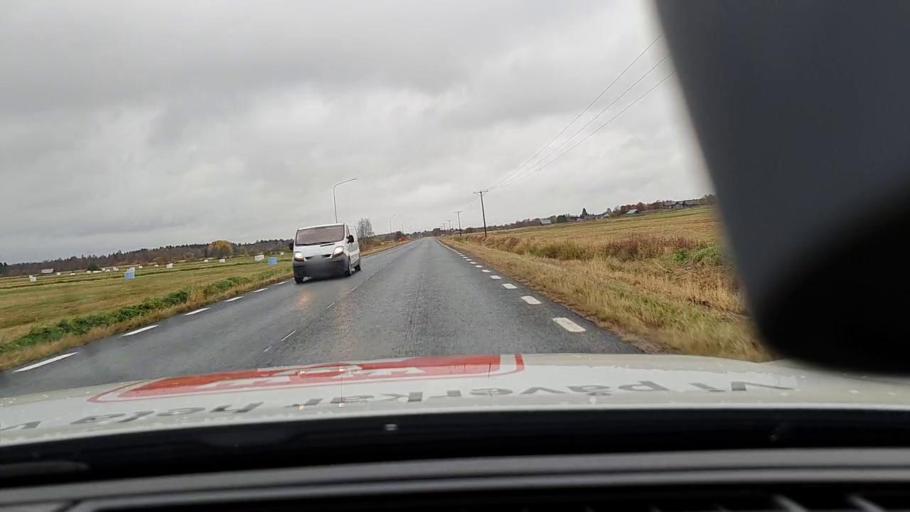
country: FI
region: Lapland
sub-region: Kemi-Tornio
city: Tornio
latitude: 65.9828
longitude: 24.0262
